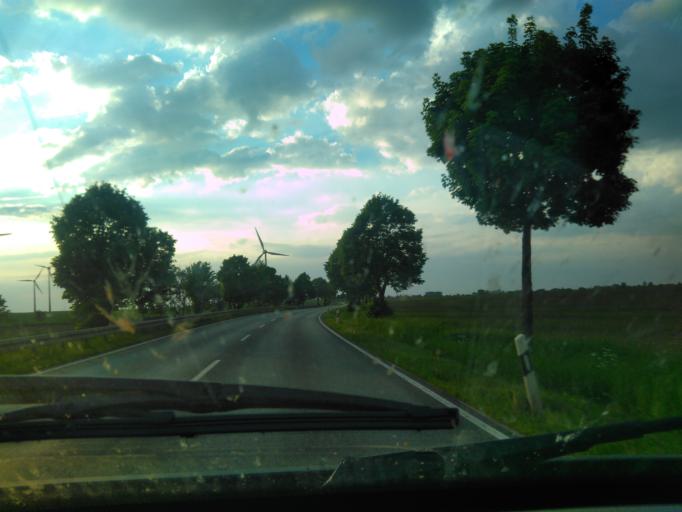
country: DE
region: Saxony-Anhalt
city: Stossen
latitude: 51.0996
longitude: 11.9395
